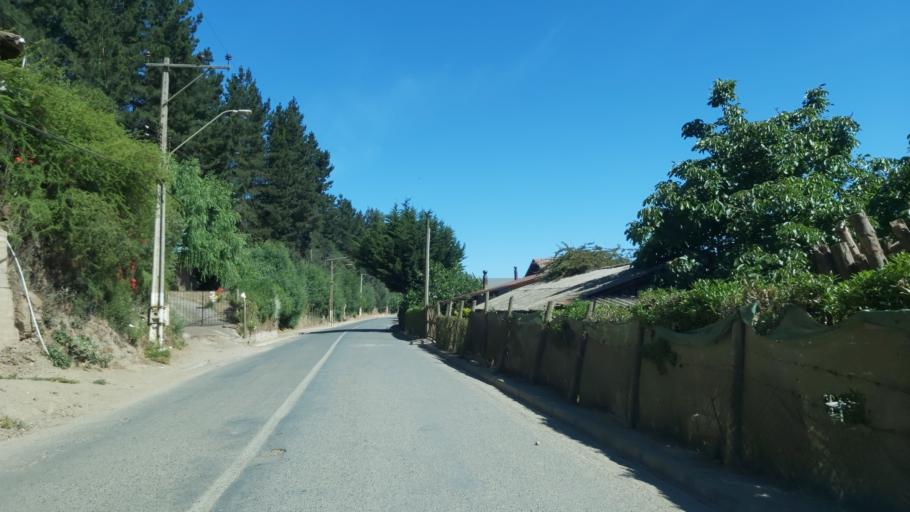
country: CL
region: Maule
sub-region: Provincia de Talca
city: Constitucion
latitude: -34.7736
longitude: -72.0651
